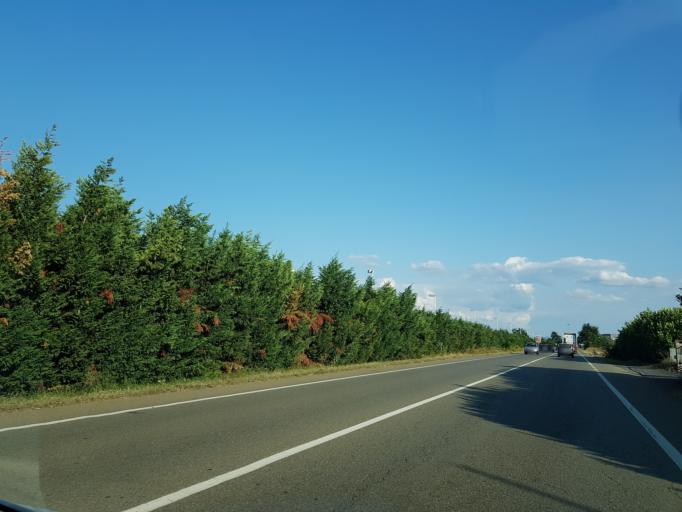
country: IT
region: Piedmont
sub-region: Provincia di Alessandria
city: Mandrogne
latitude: 44.8419
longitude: 8.7290
